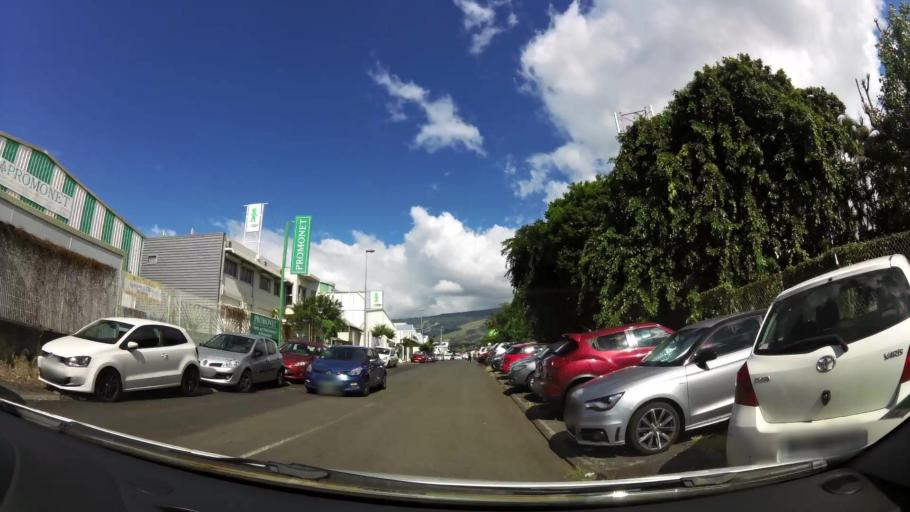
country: RE
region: Reunion
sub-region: Reunion
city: Saint-Denis
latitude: -20.8903
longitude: 55.4951
